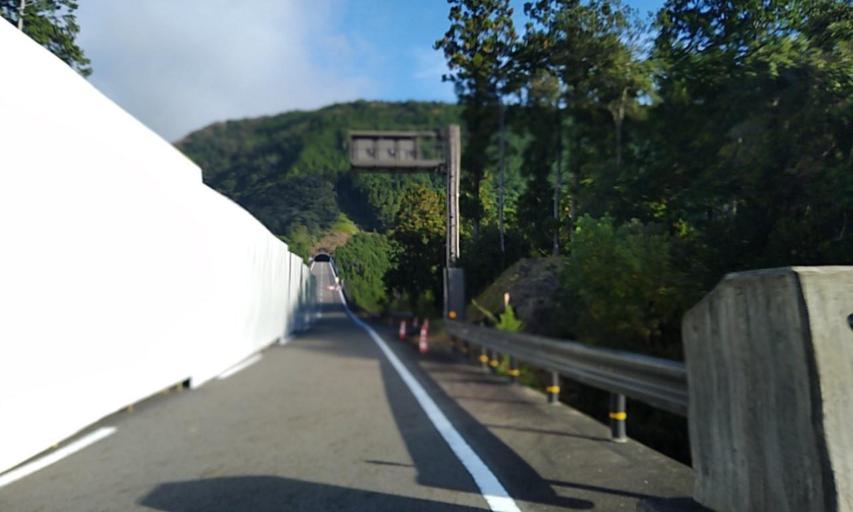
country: JP
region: Wakayama
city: Shingu
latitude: 33.8921
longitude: 135.8798
